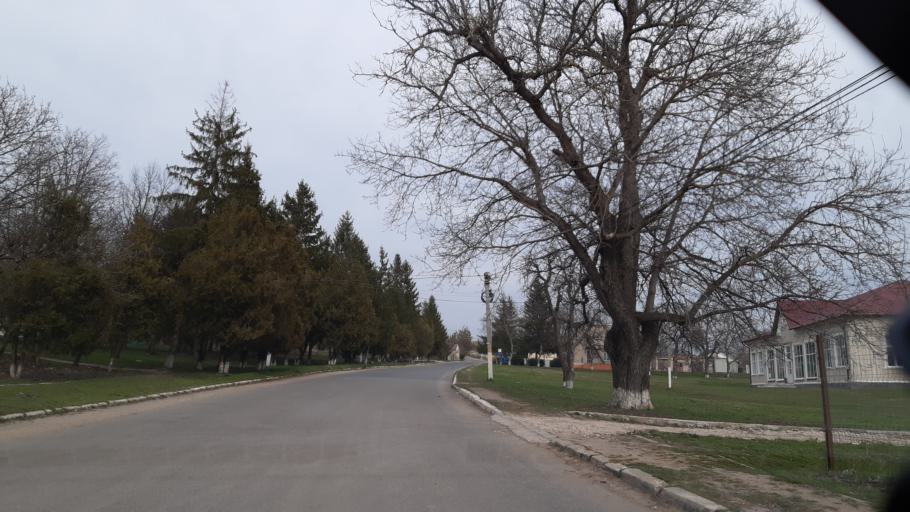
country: MD
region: Soldanesti
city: Soldanesti
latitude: 47.6841
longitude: 28.7618
